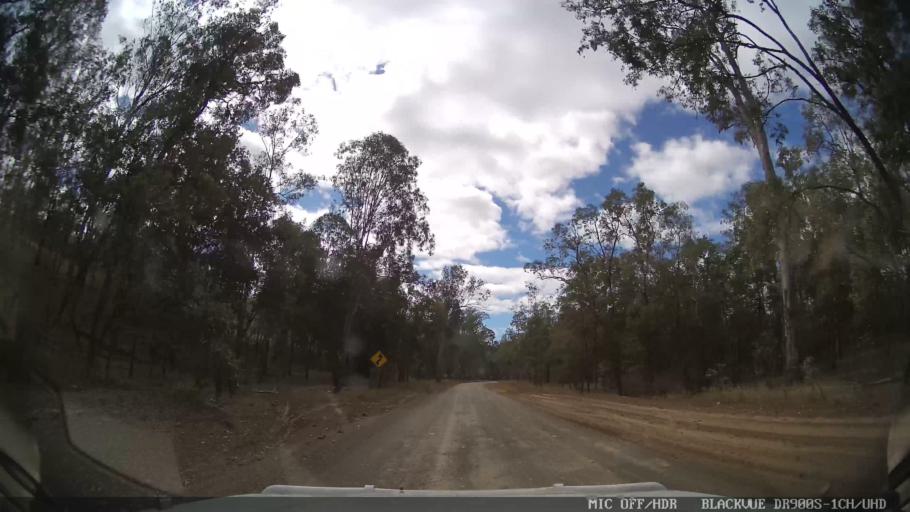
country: AU
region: Queensland
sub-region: Gladstone
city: Toolooa
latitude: -24.5488
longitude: 151.3431
